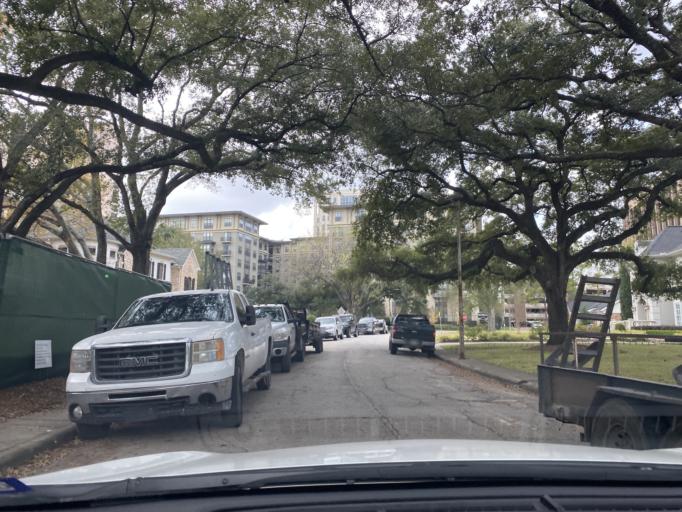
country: US
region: Texas
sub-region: Harris County
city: Hunters Creek Village
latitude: 29.7470
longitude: -95.4698
